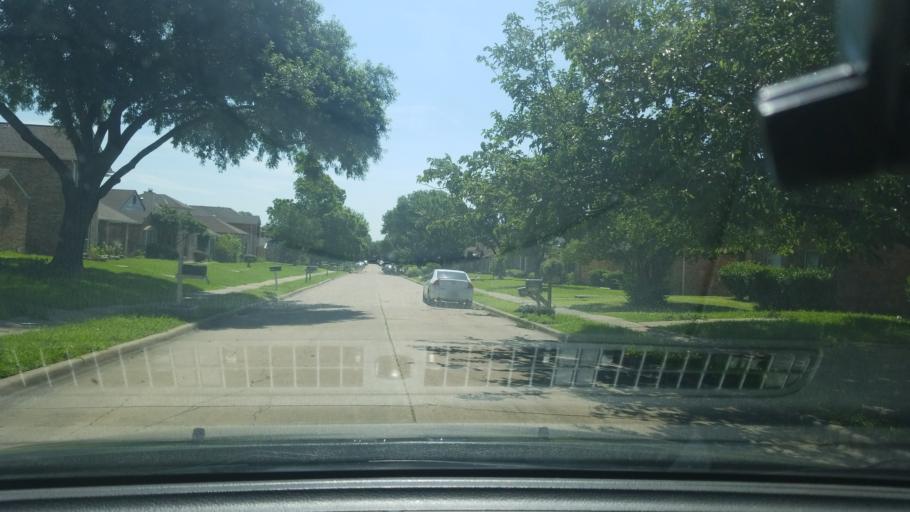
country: US
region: Texas
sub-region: Dallas County
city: Mesquite
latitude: 32.7722
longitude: -96.5849
